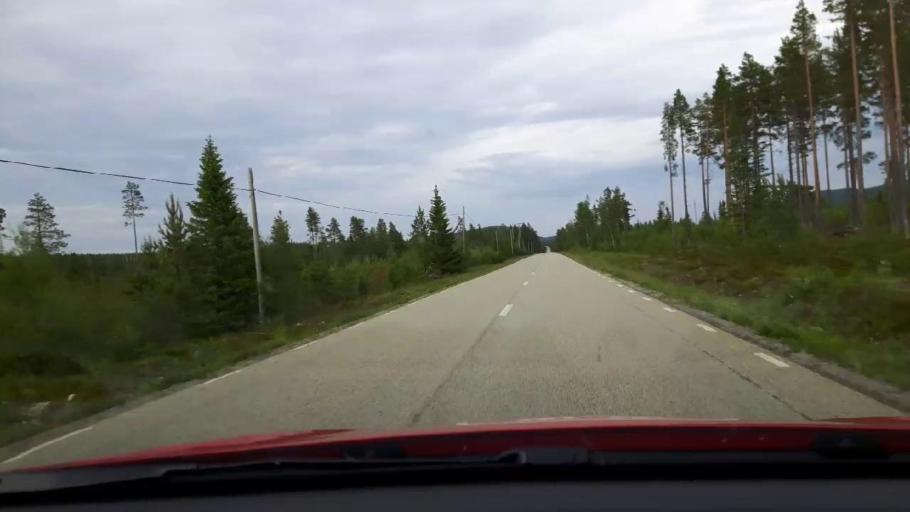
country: SE
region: Jaemtland
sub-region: Bergs Kommun
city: Hoverberg
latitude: 62.6481
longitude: 14.0882
